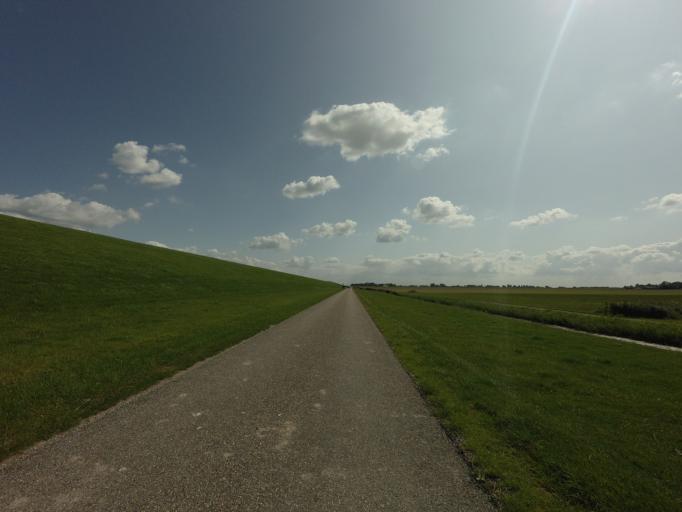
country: NL
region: Friesland
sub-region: Gemeente Ferwerderadiel
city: Hallum
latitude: 53.3221
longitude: 5.7434
